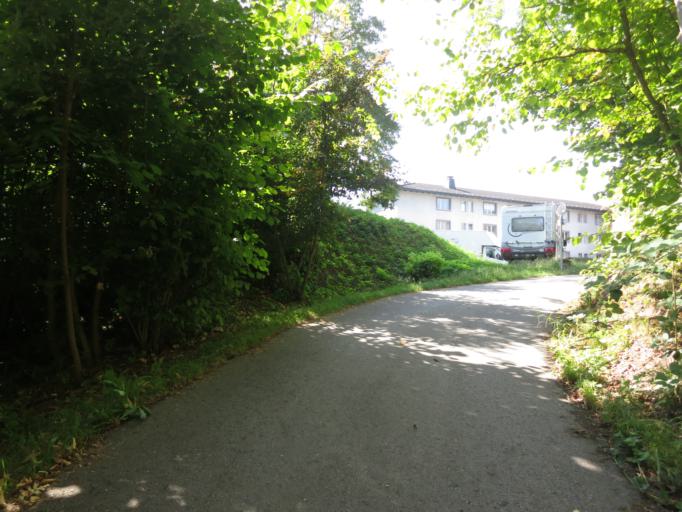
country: CH
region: Zurich
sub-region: Bezirk Meilen
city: Hombrechtikon
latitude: 47.2532
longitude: 8.7779
